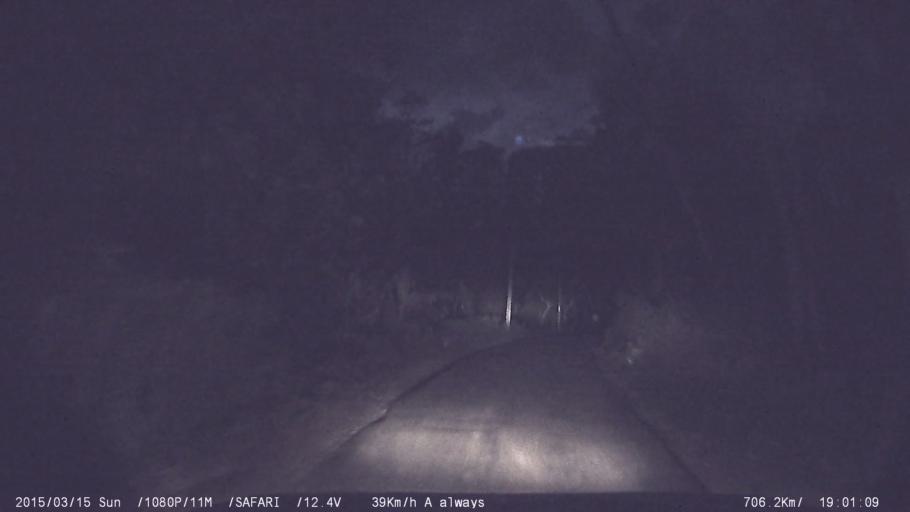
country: IN
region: Kerala
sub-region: Kottayam
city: Palackattumala
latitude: 9.8740
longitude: 76.6543
